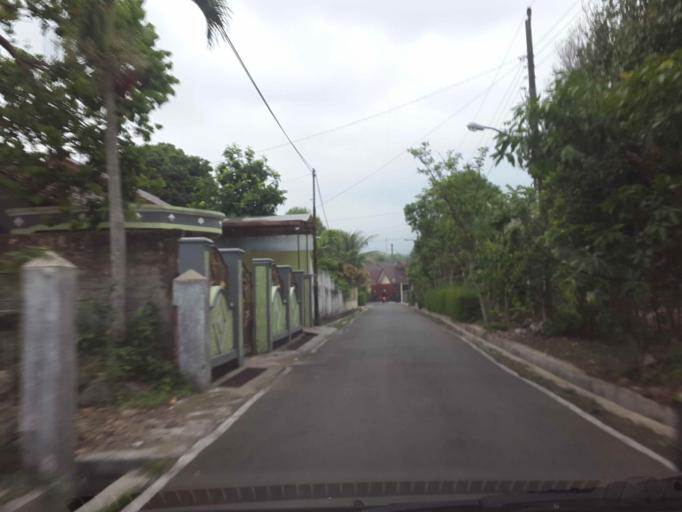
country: ID
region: Central Java
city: Salatiga
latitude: -7.3346
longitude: 110.4955
